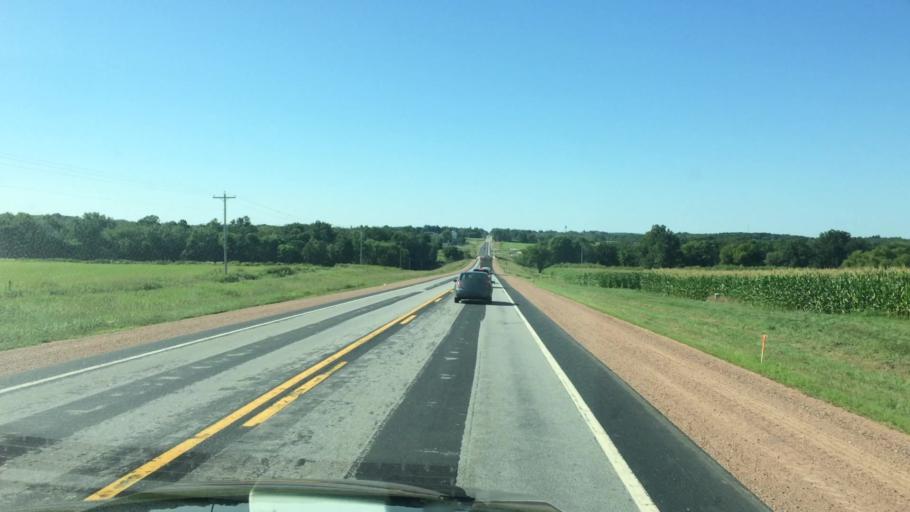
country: US
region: Wisconsin
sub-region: Marathon County
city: Stratford
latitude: 44.8272
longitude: -90.0792
